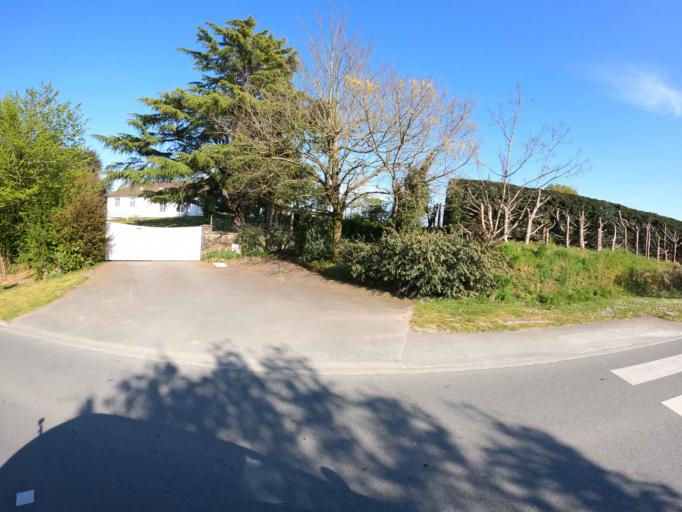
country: FR
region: Pays de la Loire
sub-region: Departement de la Vendee
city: Mortagne-sur-Sevre
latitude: 46.9989
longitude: -0.9421
